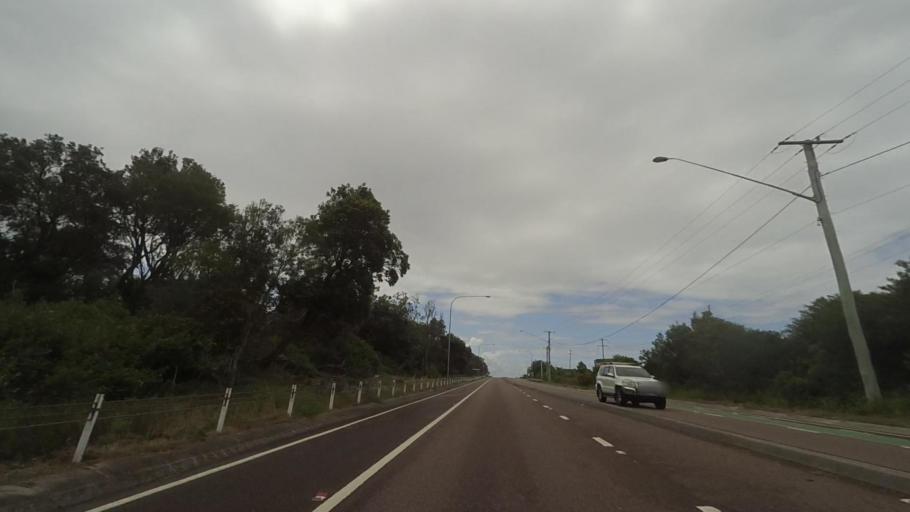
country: AU
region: New South Wales
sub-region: Wyong Shire
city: The Entrance
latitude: -33.3128
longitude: 151.5196
